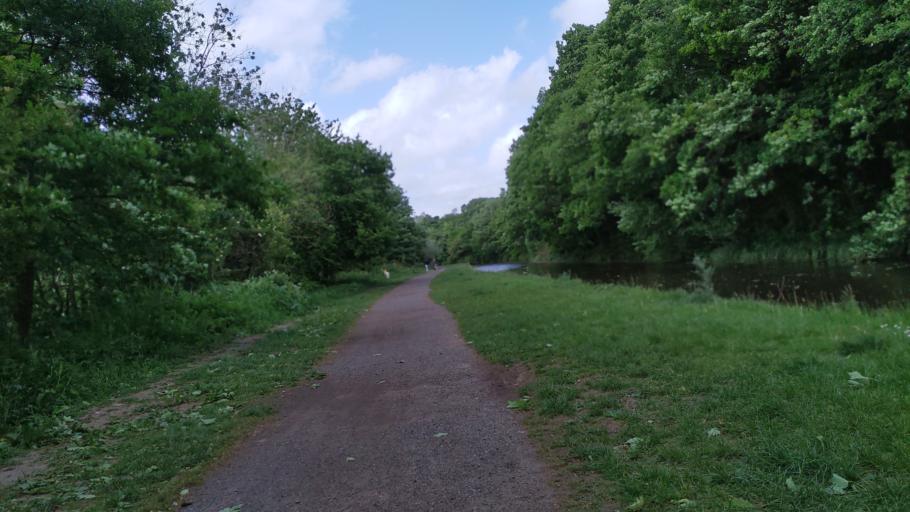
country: GB
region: England
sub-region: Lancashire
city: Chorley
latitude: 53.6492
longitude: -2.6115
